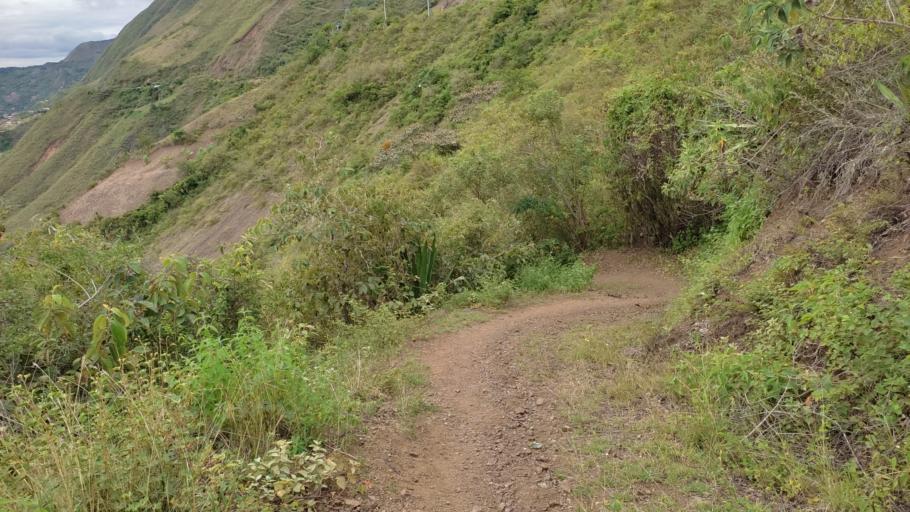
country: CO
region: Narino
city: Taminango
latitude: 1.5422
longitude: -77.3677
